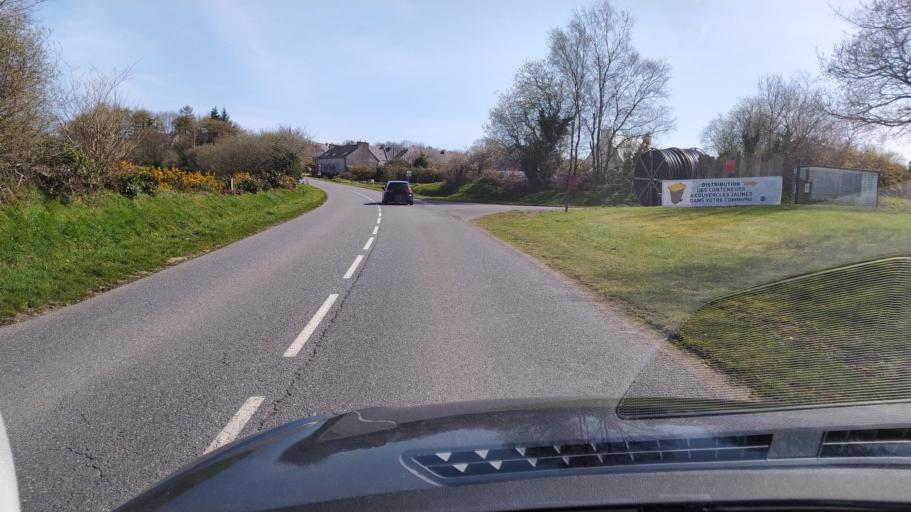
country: FR
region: Brittany
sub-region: Departement du Finistere
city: Plouneour-Menez
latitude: 48.4166
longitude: -3.9661
